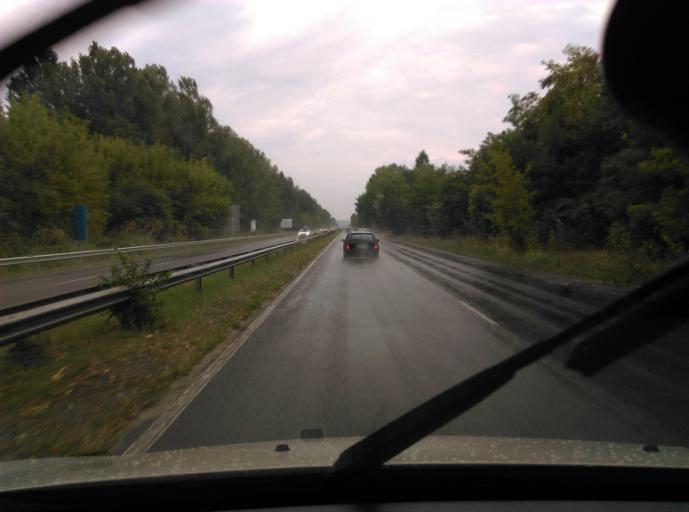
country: BG
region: Burgas
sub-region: Obshtina Burgas
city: Burgas
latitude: 42.4683
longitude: 27.4372
